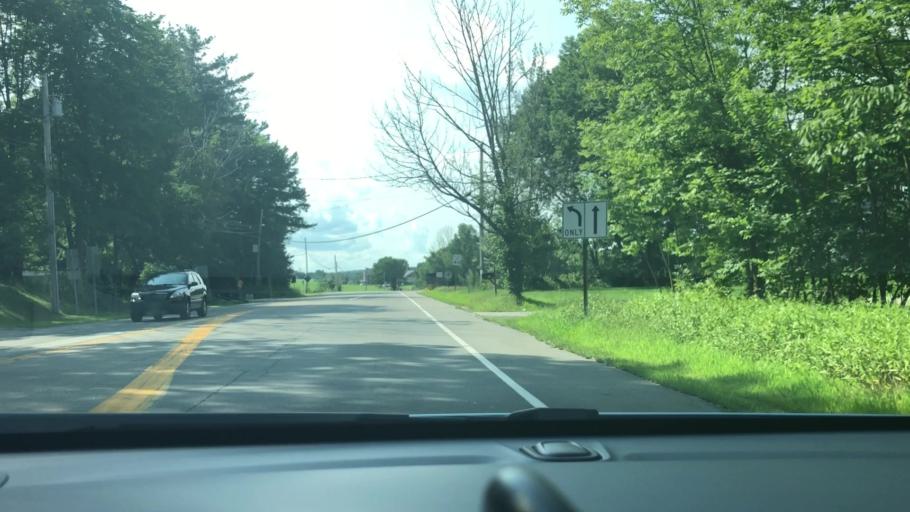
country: US
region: New Hampshire
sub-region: Hillsborough County
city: Pinardville
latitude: 43.0069
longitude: -71.5287
